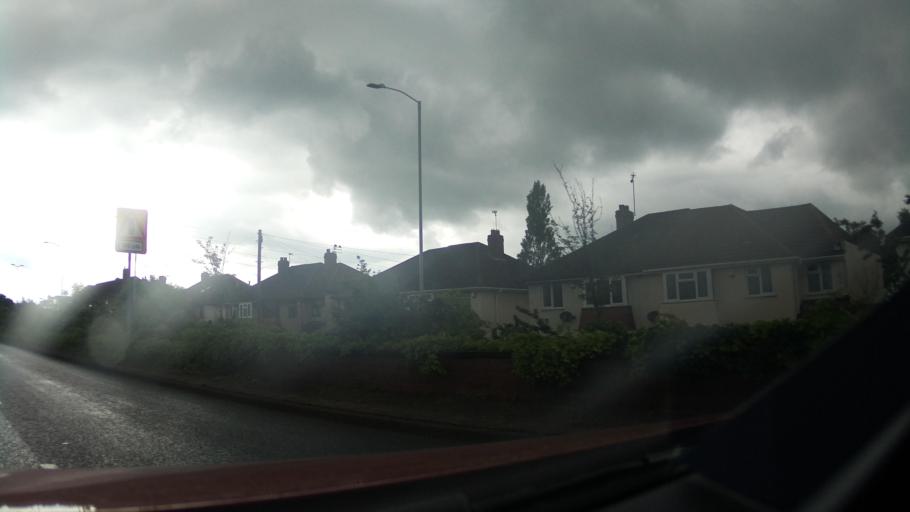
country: GB
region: England
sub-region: Wolverhampton
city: Wolverhampton
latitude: 52.5567
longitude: -2.1677
